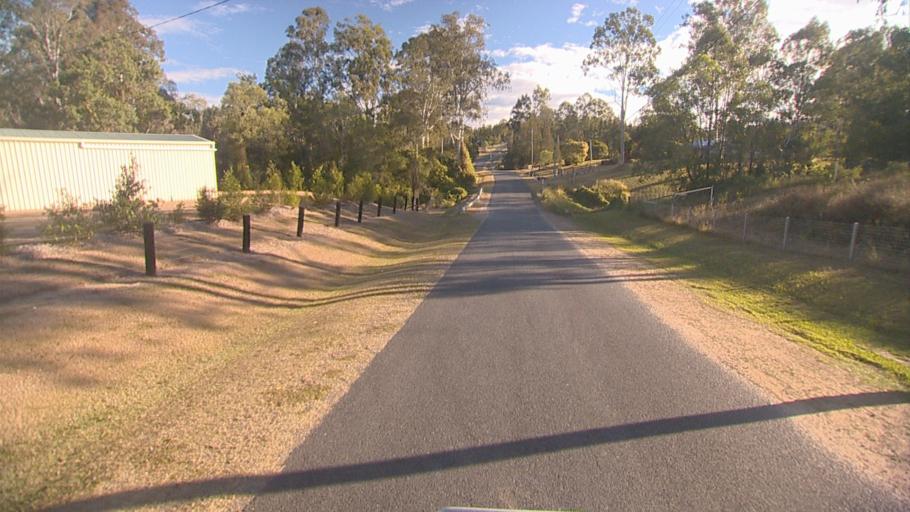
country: AU
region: Queensland
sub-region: Logan
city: Cedar Vale
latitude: -27.9286
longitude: 153.0685
